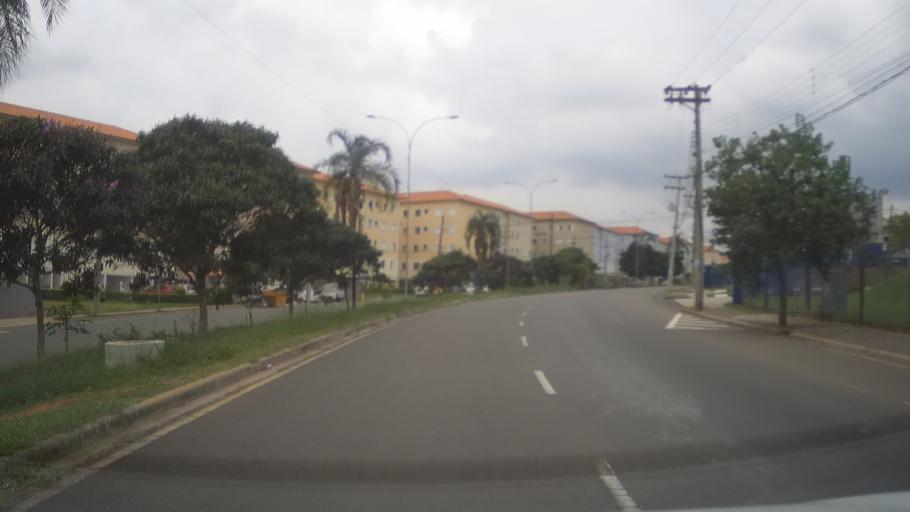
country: BR
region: Sao Paulo
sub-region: Itupeva
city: Itupeva
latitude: -23.1529
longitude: -47.0119
